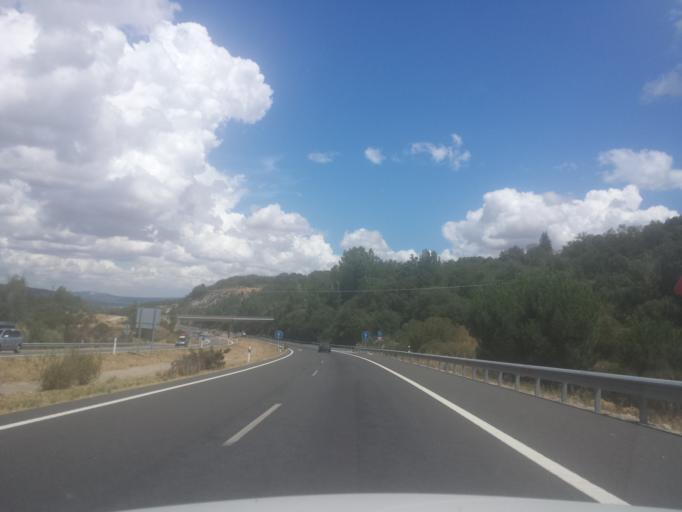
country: ES
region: Castille and Leon
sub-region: Provincia de Salamanca
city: Puerto de Bejar
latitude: 40.3482
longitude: -5.8448
